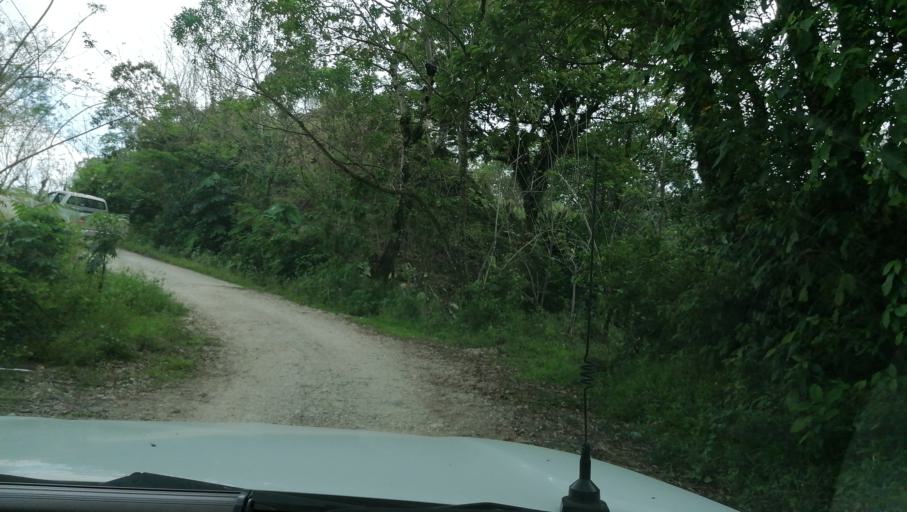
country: MX
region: Chiapas
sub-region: Ocotepec
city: San Pablo Huacano
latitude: 17.2704
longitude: -93.2433
